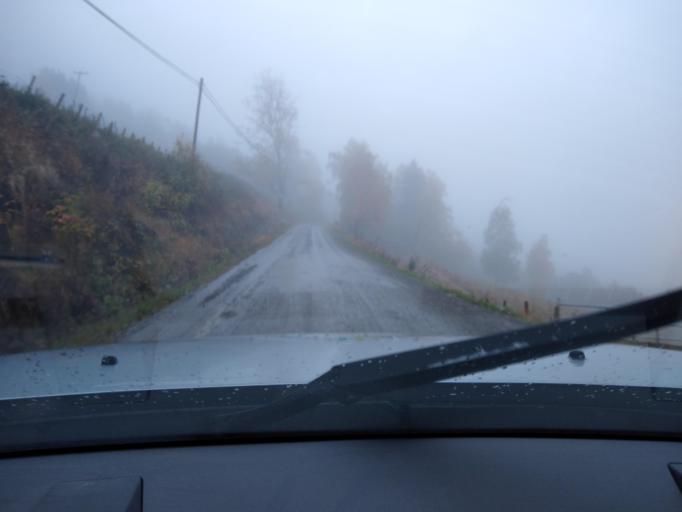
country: NO
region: Oppland
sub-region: Ringebu
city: Ringebu
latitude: 61.5279
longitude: 10.1582
